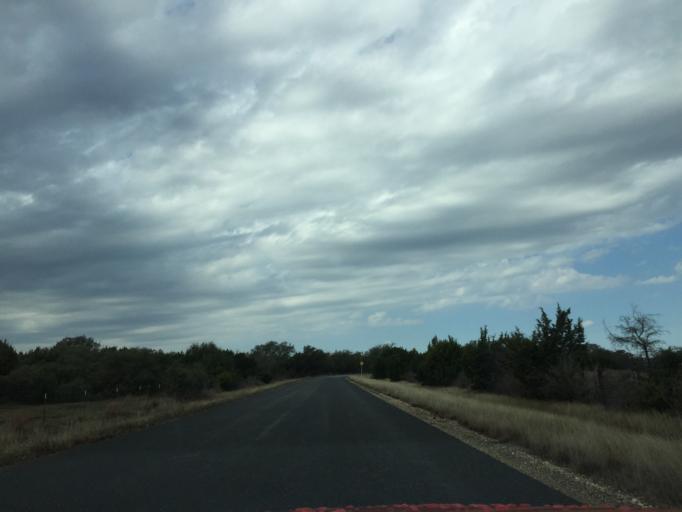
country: US
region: Texas
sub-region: Burnet County
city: Bertram
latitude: 30.6281
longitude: -97.9944
